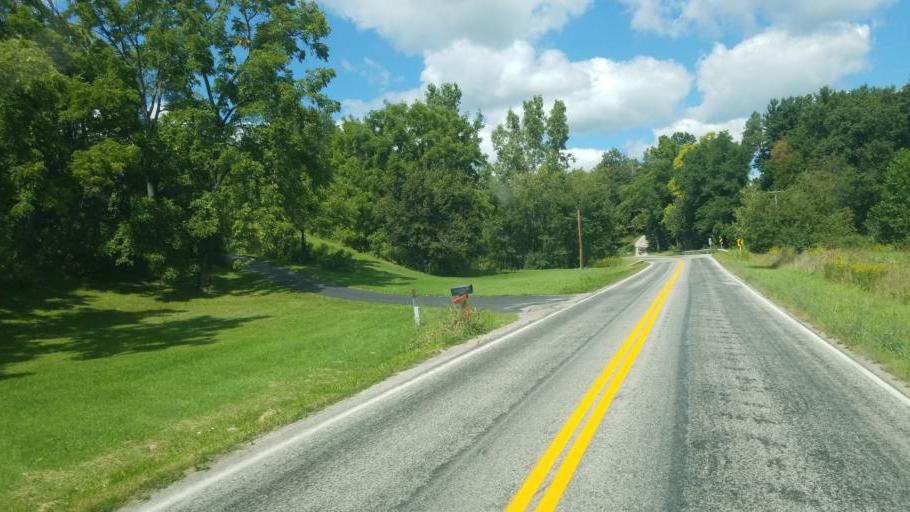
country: US
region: Ohio
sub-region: Ashland County
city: Ashland
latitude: 40.9386
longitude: -82.2818
